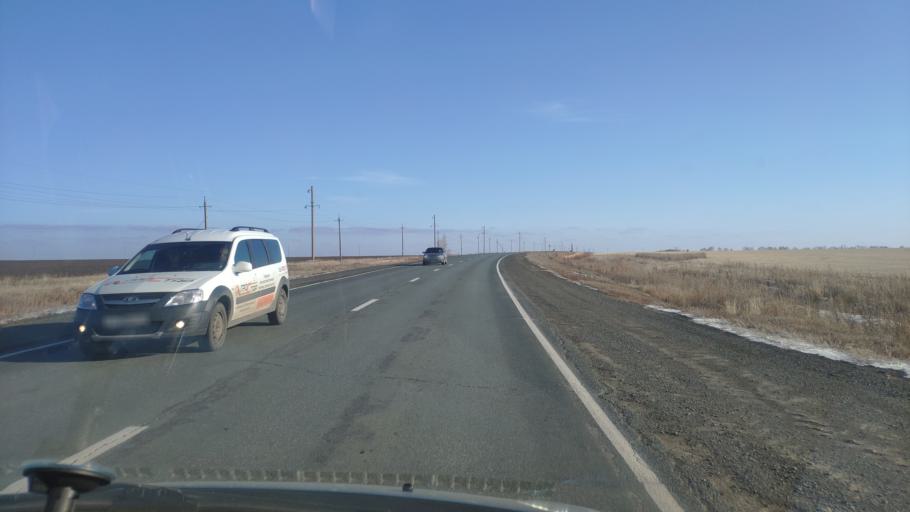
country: RU
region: Orenburg
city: Novorudnyy
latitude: 51.4352
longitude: 57.8971
